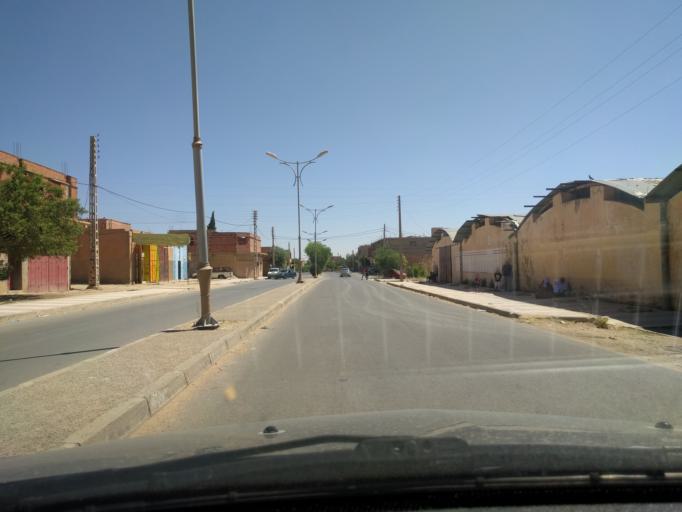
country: DZ
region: Tiaret
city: Frenda
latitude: 34.8902
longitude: 1.2440
